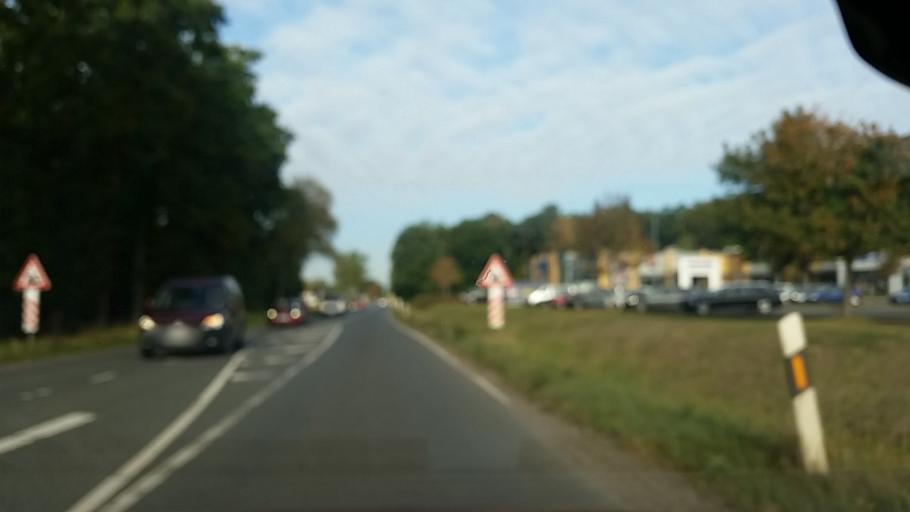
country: DE
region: Lower Saxony
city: Lachendorf
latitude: 52.6299
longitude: 10.2322
